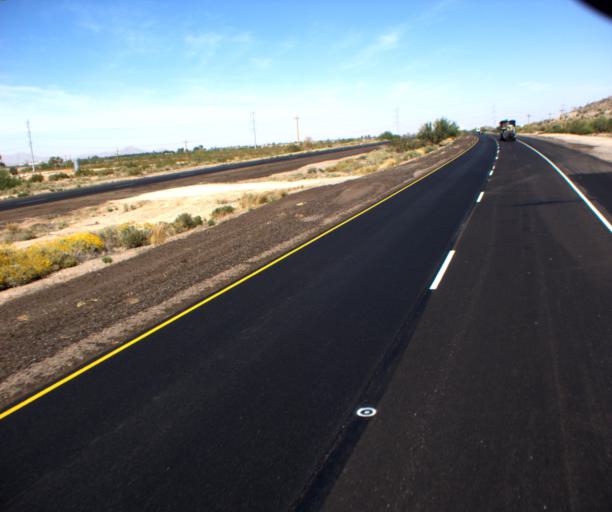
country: US
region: Arizona
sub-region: Pinal County
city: Casa Grande
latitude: 32.8306
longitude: -111.7329
